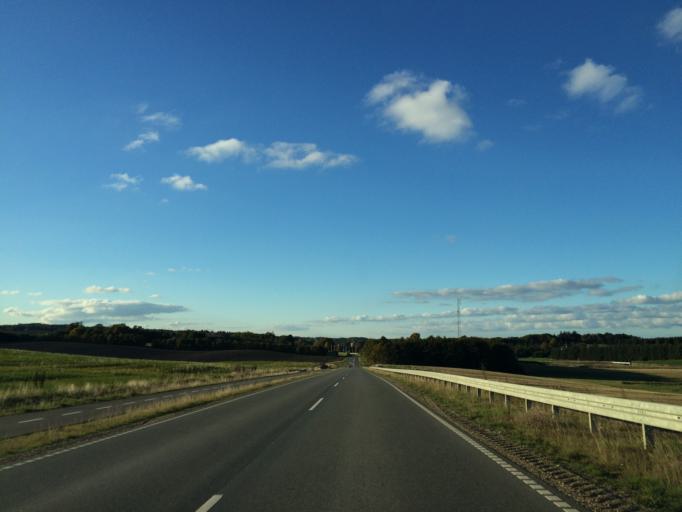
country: DK
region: Central Jutland
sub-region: Silkeborg Kommune
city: Svejbaek
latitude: 56.1479
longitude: 9.7027
